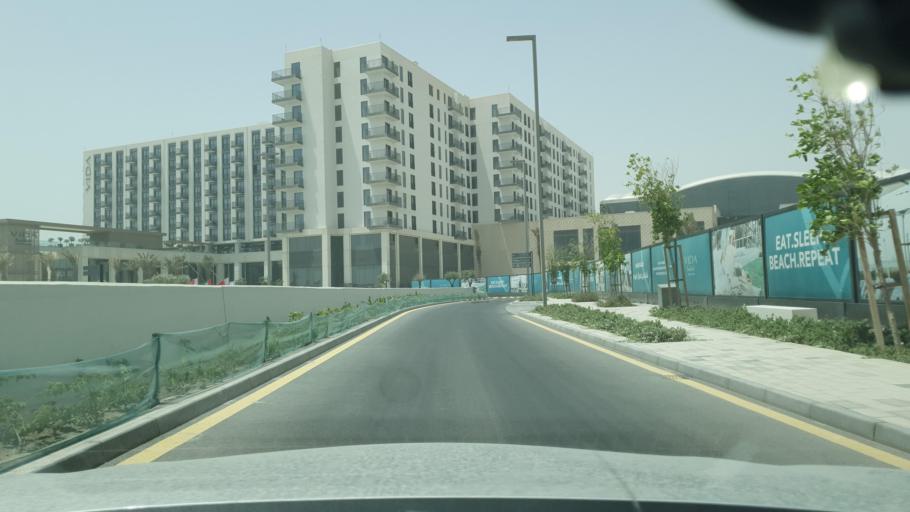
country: BH
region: Muharraq
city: Al Muharraq
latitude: 26.3051
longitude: 50.6454
